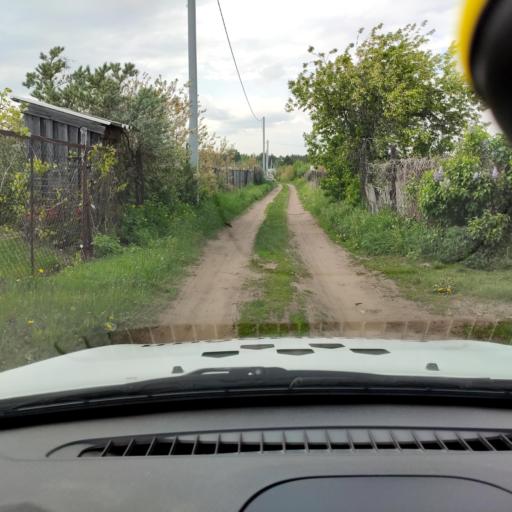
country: RU
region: Samara
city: Zhigulevsk
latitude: 53.5287
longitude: 49.5612
